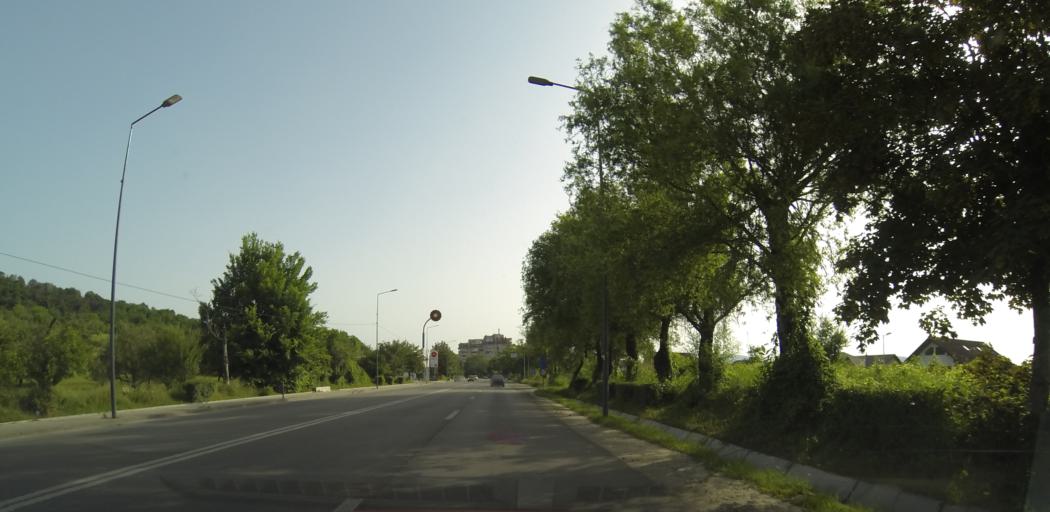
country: RO
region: Valcea
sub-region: Municipiul Ramnicu Valcea
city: Ramnicu Valcea
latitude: 45.0874
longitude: 24.3593
